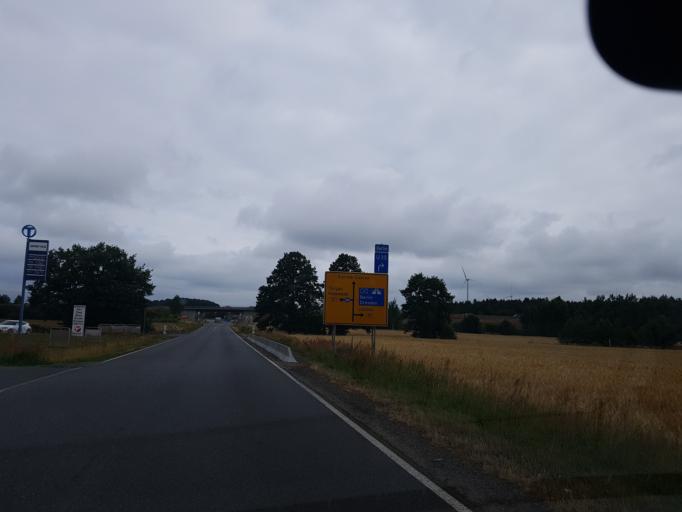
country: DE
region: Brandenburg
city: Luckau
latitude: 51.8615
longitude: 13.7356
